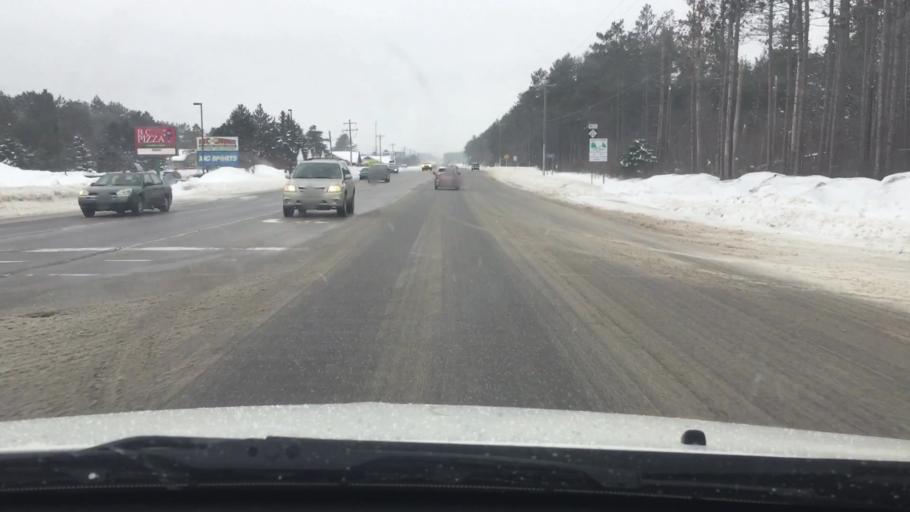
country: US
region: Michigan
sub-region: Otsego County
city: Gaylord
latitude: 45.0275
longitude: -84.7043
